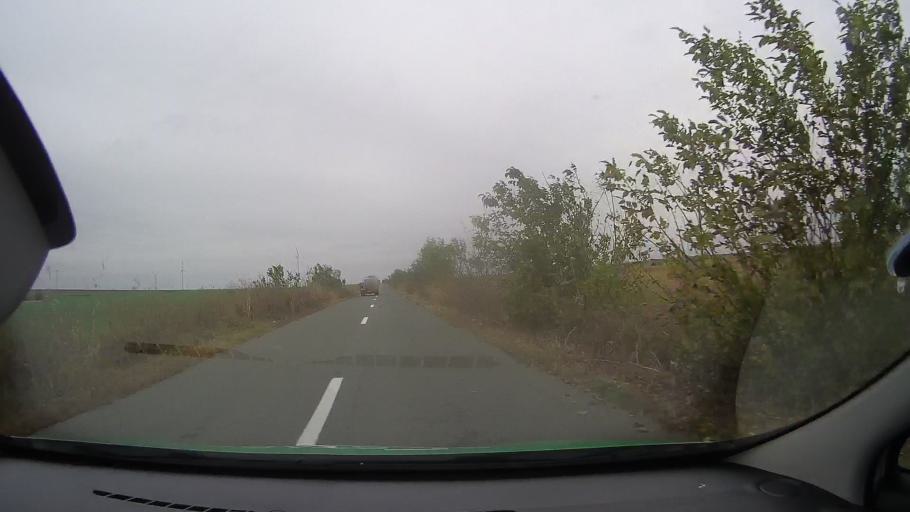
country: RO
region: Constanta
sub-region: Comuna Targusor
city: Targusor
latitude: 44.4708
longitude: 28.3875
